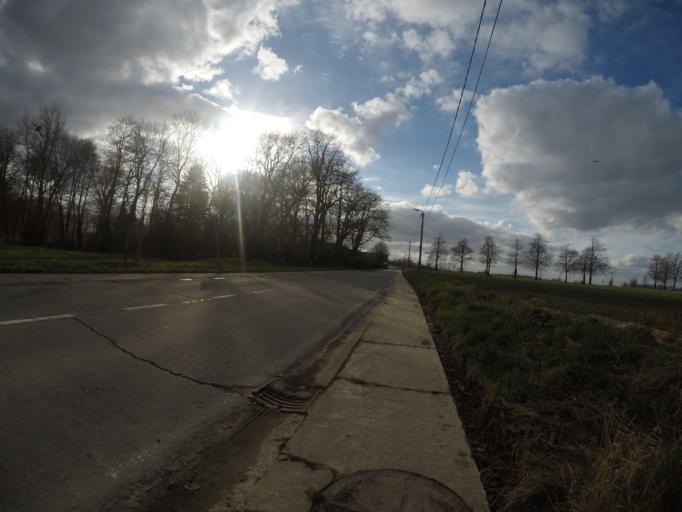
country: BE
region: Flanders
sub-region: Provincie Vlaams-Brabant
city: Pepingen
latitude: 50.7287
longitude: 4.1531
